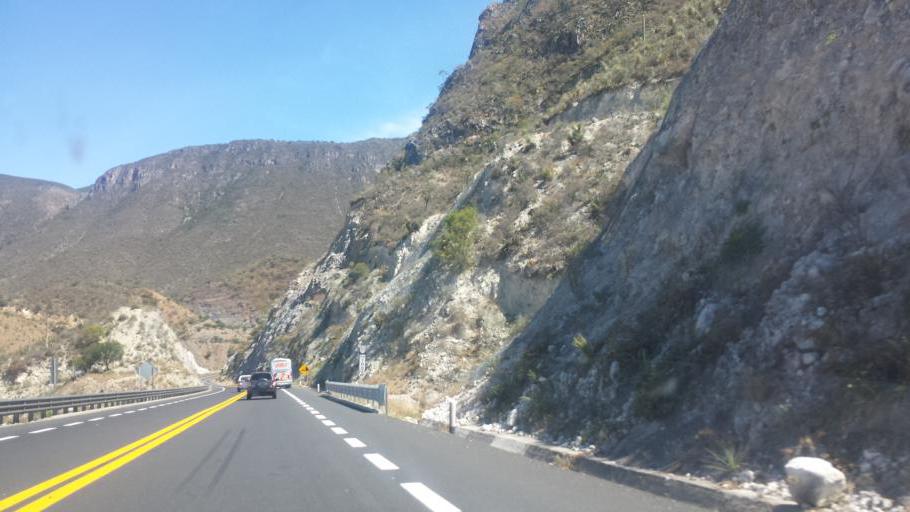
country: MX
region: Puebla
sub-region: San Jose Miahuatlan
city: San Pedro Tetitlan
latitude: 18.0886
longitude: -97.3478
